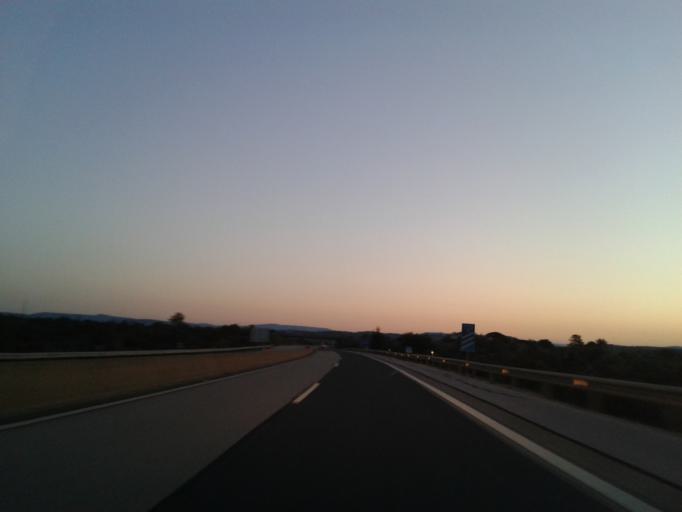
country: PT
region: Faro
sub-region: Albufeira
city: Ferreiras
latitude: 37.1454
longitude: -8.2207
